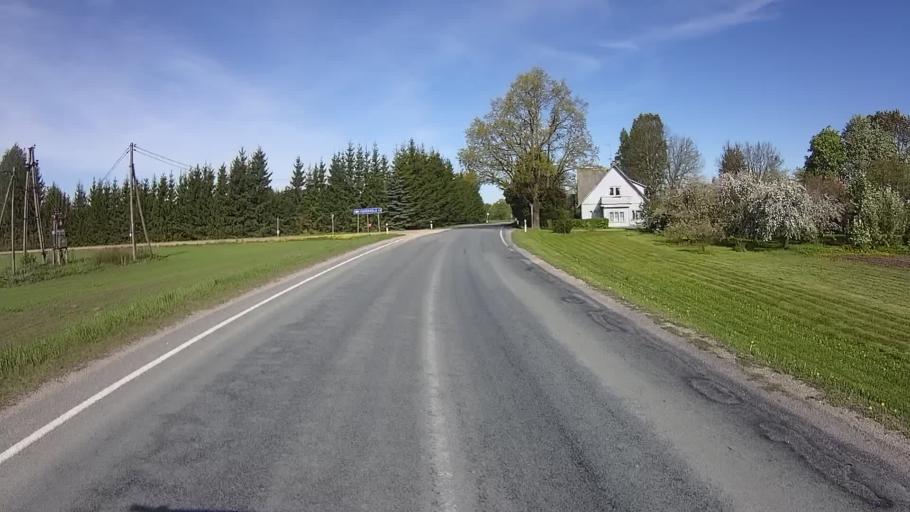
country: EE
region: Polvamaa
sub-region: Polva linn
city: Polva
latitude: 58.2258
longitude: 27.0303
